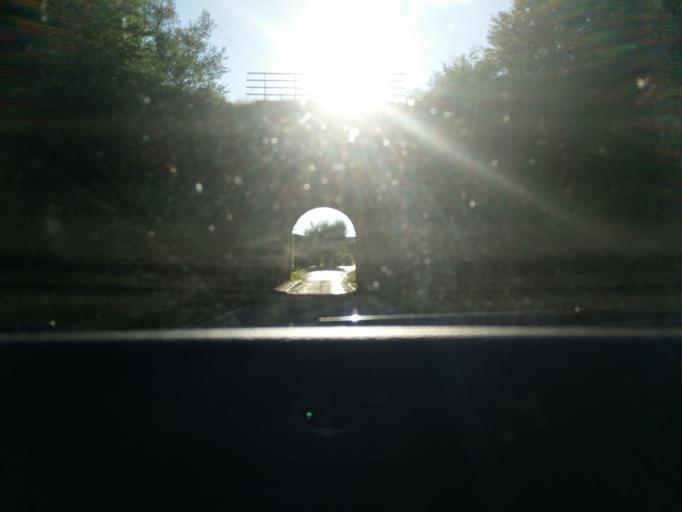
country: BE
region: Wallonia
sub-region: Province du Hainaut
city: Beaumont
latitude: 50.2330
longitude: 4.2432
